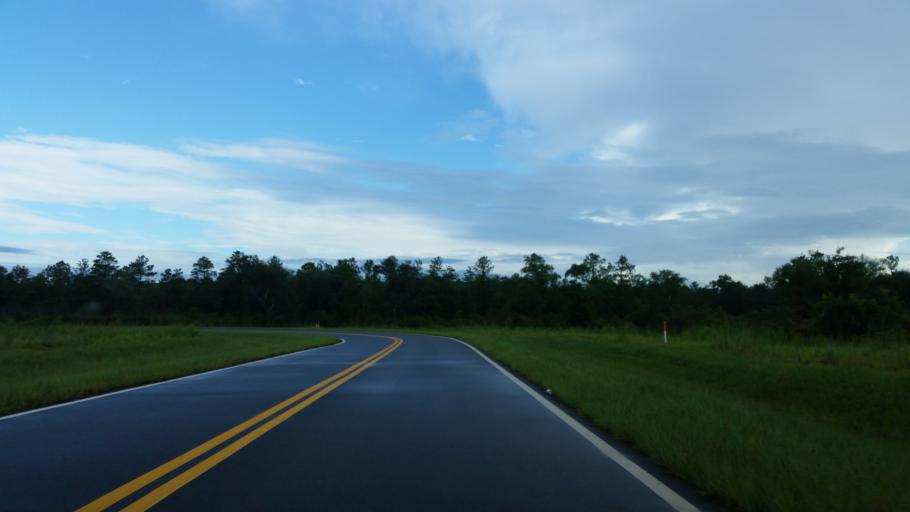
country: US
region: Florida
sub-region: Walton County
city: DeFuniak Springs
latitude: 30.7386
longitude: -86.3292
